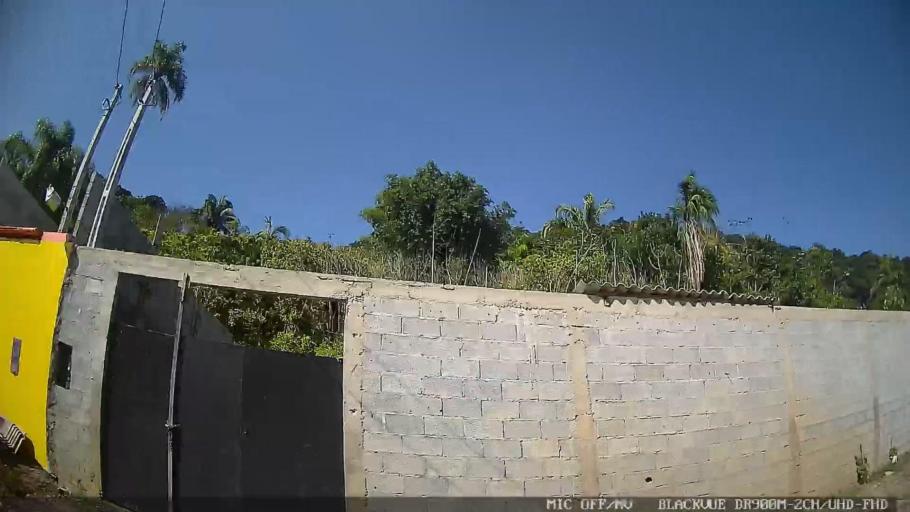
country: BR
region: Sao Paulo
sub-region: Guaruja
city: Guaruja
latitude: -24.0083
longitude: -46.2887
